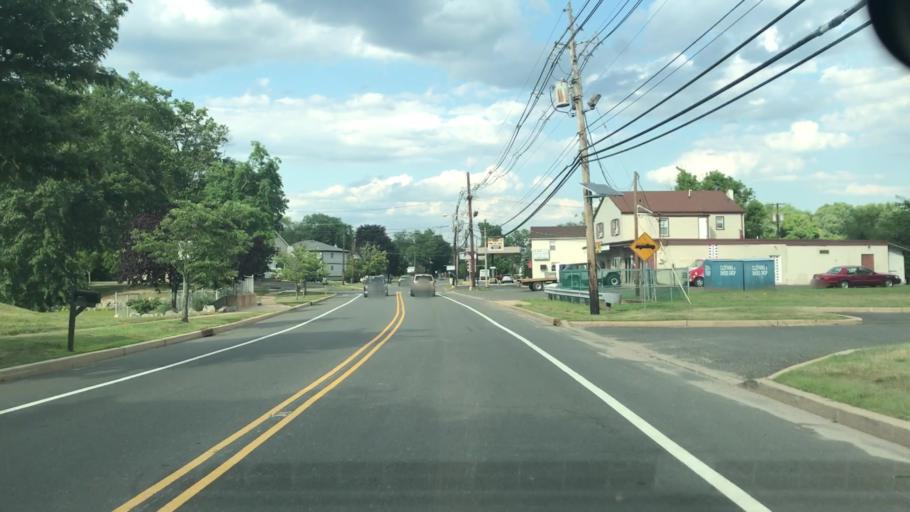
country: US
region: New Jersey
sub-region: Somerset County
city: Bradley Gardens
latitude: 40.5591
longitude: -74.6537
